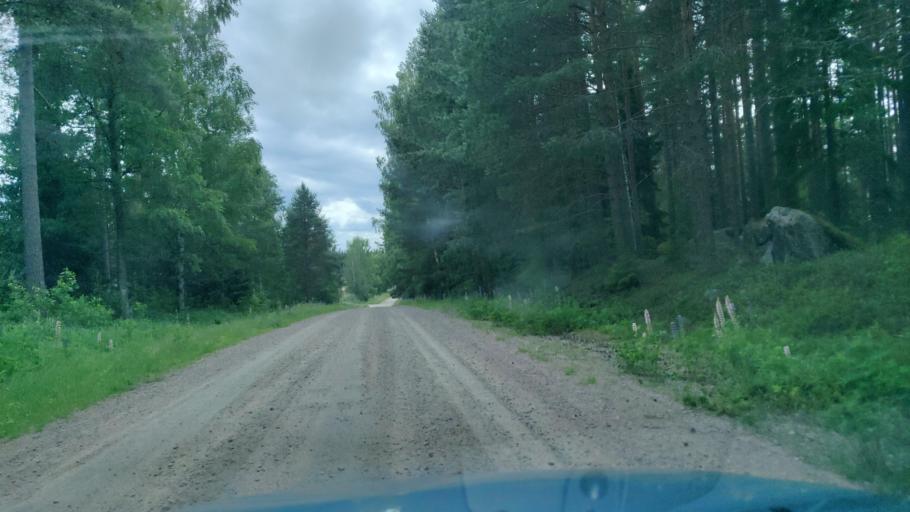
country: SE
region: Vaermland
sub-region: Hagfors Kommun
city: Hagfors
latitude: 60.0327
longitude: 13.7153
